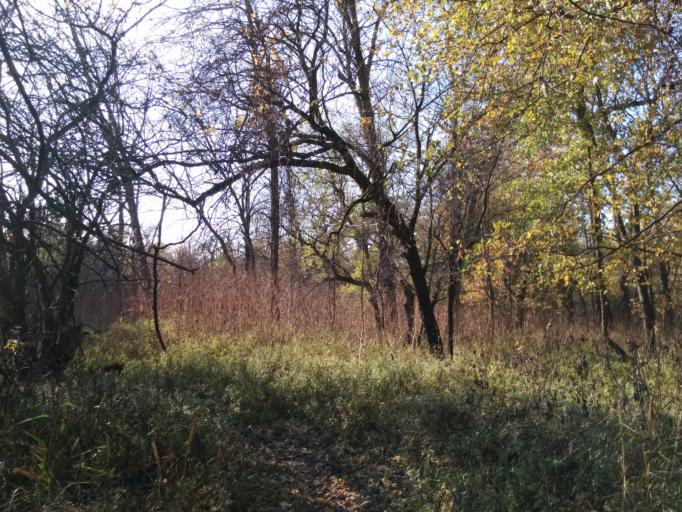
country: US
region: Illinois
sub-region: Cook County
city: River Forest
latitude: 41.8936
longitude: -87.8288
